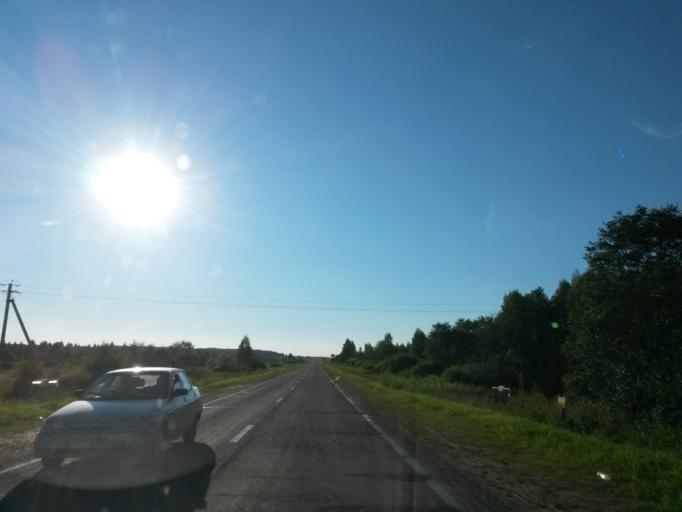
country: RU
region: Jaroslavl
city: Gavrilov-Yam
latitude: 57.2792
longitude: 39.9174
